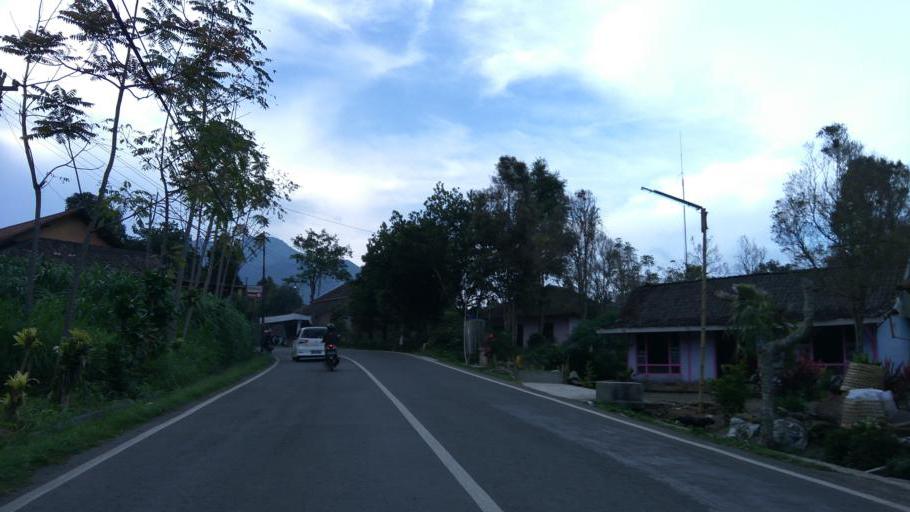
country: ID
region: Central Java
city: Gunung Kendil
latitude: -7.3766
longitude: 110.4336
